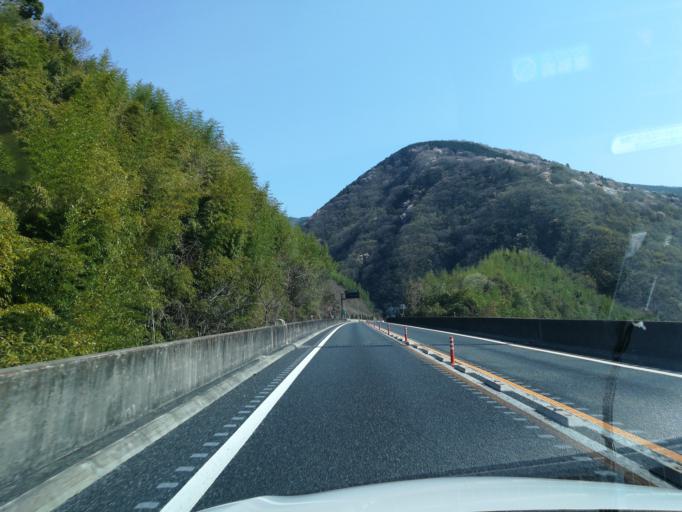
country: JP
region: Tokushima
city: Ikedacho
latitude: 34.0485
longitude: 133.9141
